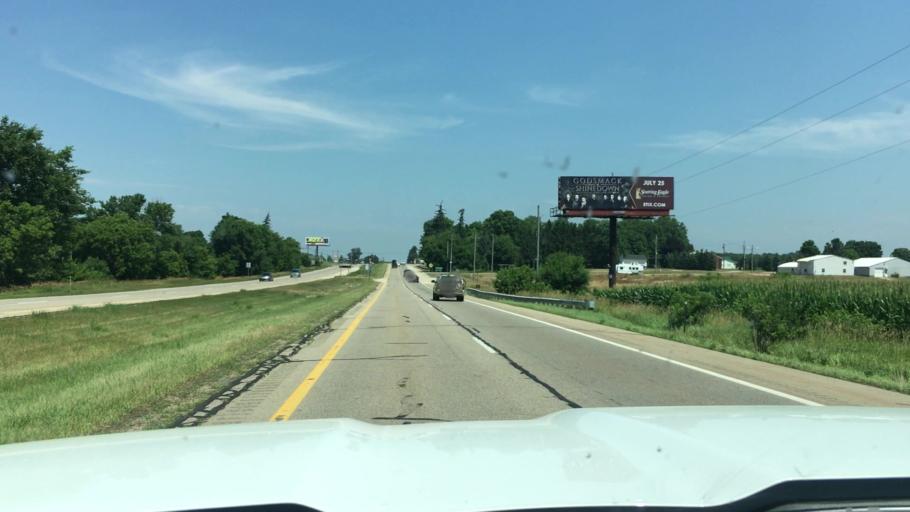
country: US
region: Michigan
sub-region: Clinton County
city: Saint Johns
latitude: 43.0562
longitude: -84.5638
